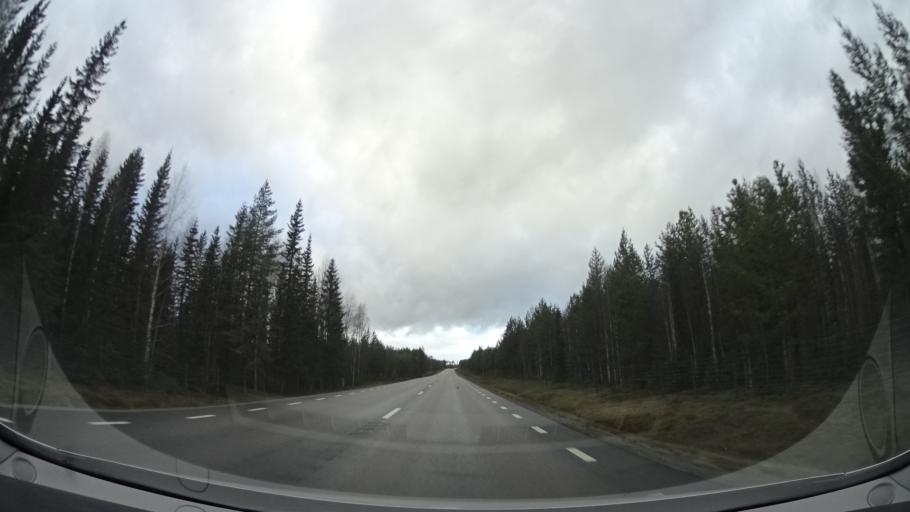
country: SE
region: Vaesterbotten
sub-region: Skelleftea Kommun
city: Viken
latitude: 64.7885
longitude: 20.7758
